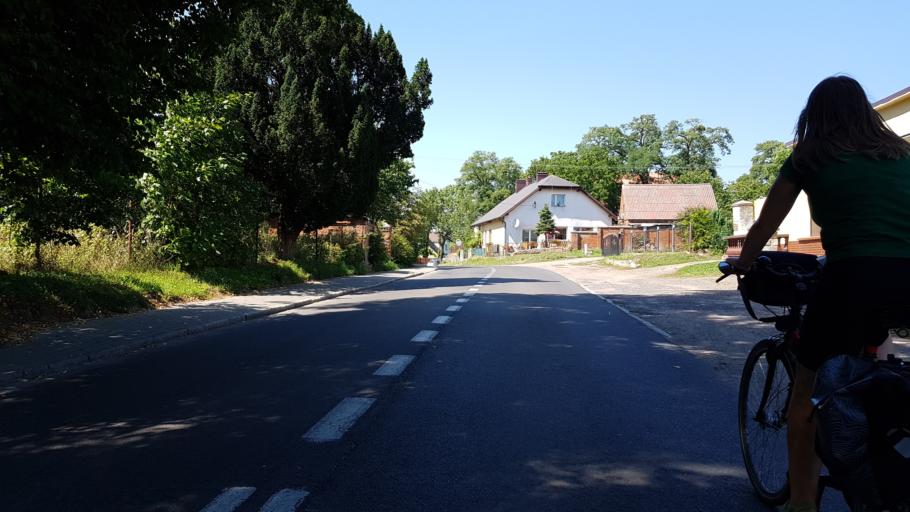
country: PL
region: West Pomeranian Voivodeship
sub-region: Powiat gryfinski
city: Banie
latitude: 53.1633
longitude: 14.5941
